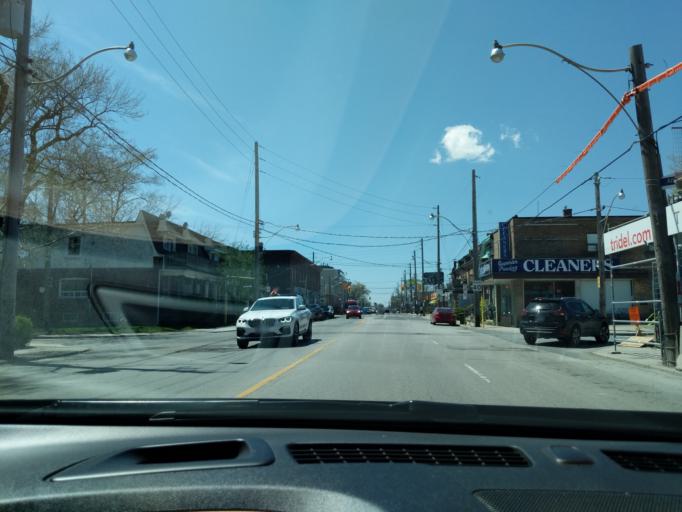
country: CA
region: Ontario
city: Toronto
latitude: 43.6734
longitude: -79.4131
